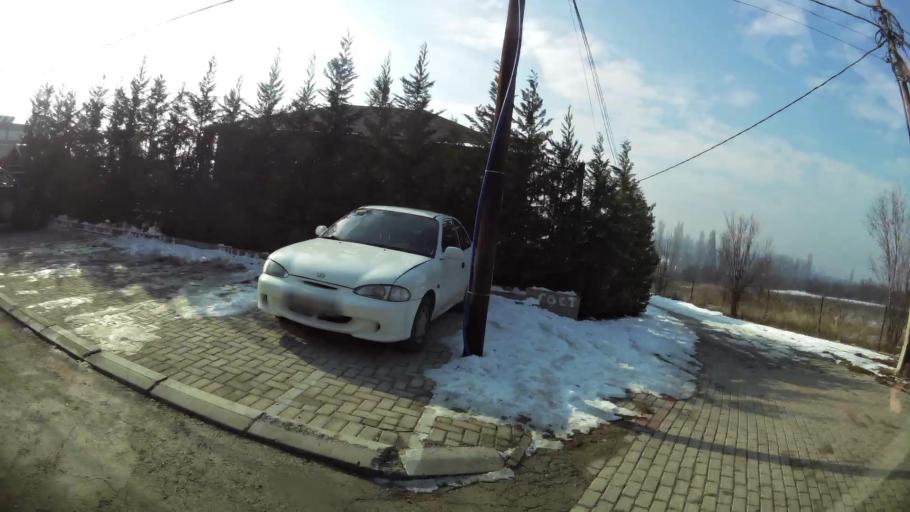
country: MK
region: Suto Orizari
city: Suto Orizare
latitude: 42.0313
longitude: 21.3767
